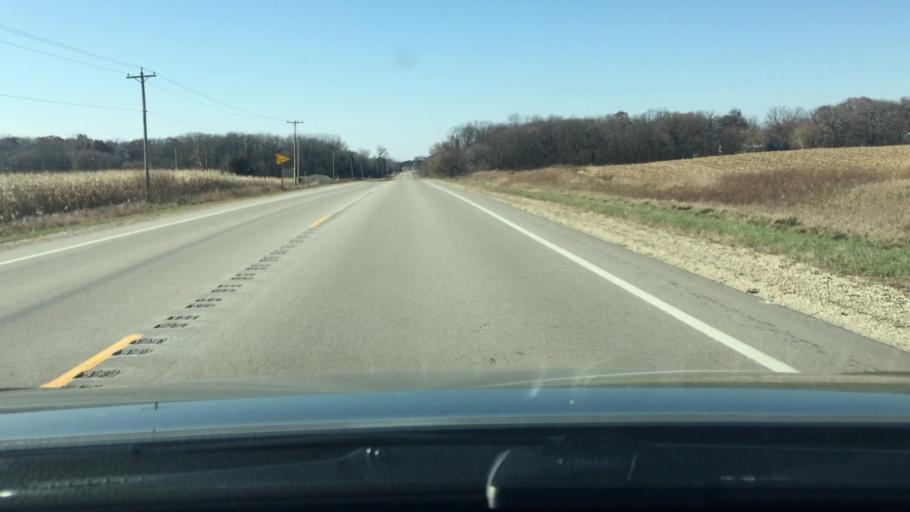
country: US
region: Wisconsin
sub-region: Jefferson County
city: Lake Ripley
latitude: 43.0077
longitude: -88.9319
